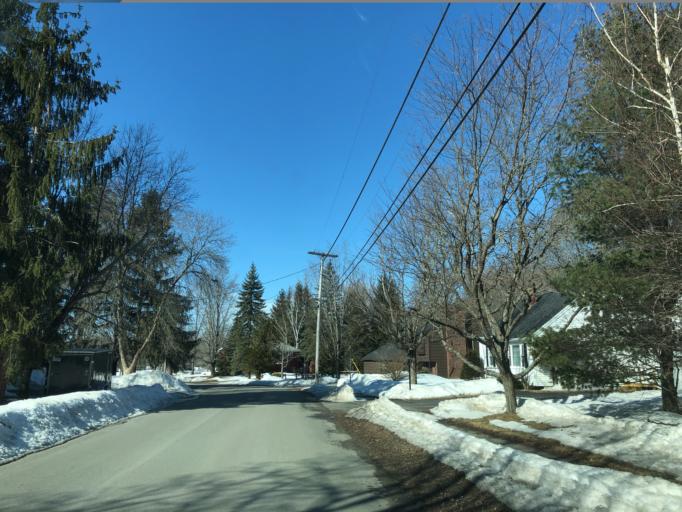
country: US
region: Maine
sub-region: Penobscot County
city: Brewer
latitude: 44.8213
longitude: -68.7559
